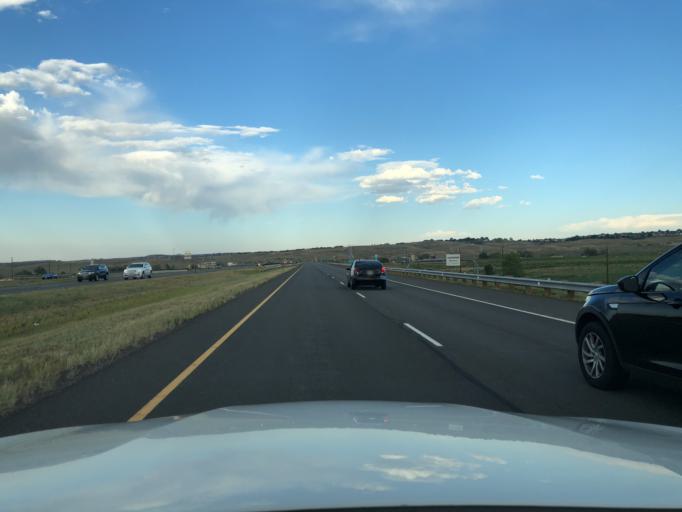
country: US
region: Colorado
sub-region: Boulder County
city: Lafayette
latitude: 39.9582
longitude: -105.0993
